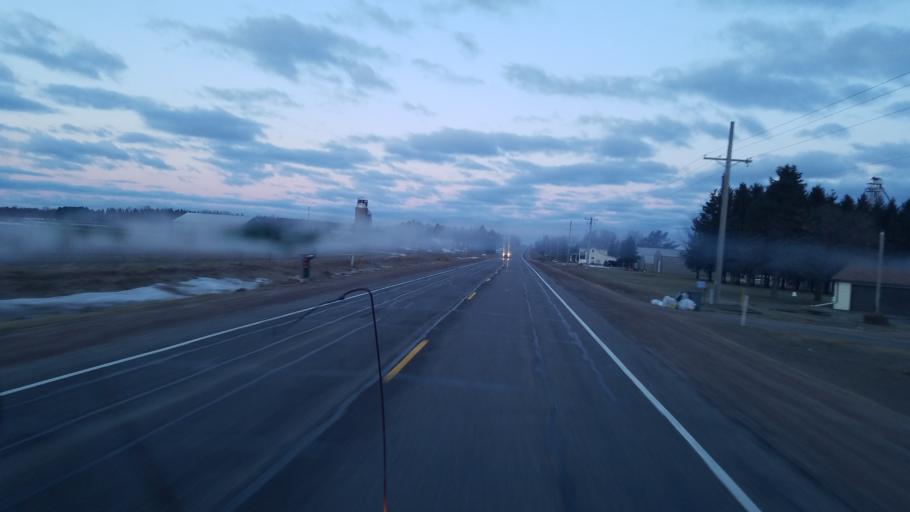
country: US
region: Wisconsin
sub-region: Clark County
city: Loyal
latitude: 44.5821
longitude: -90.4247
